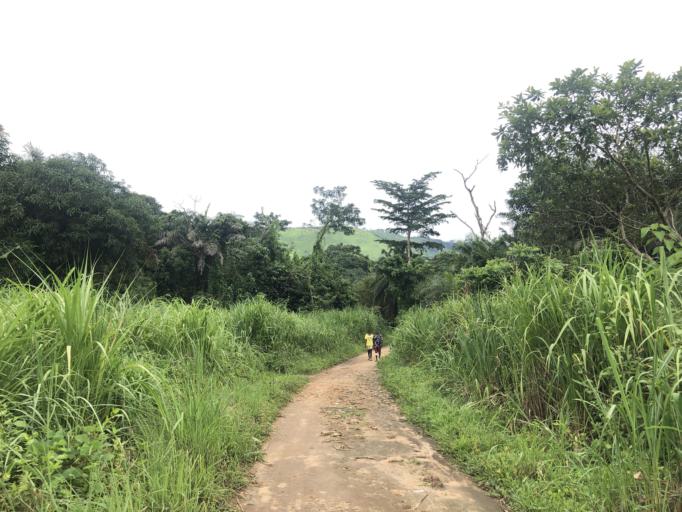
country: SL
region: Northern Province
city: Bumbuna
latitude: 8.9956
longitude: -11.7558
